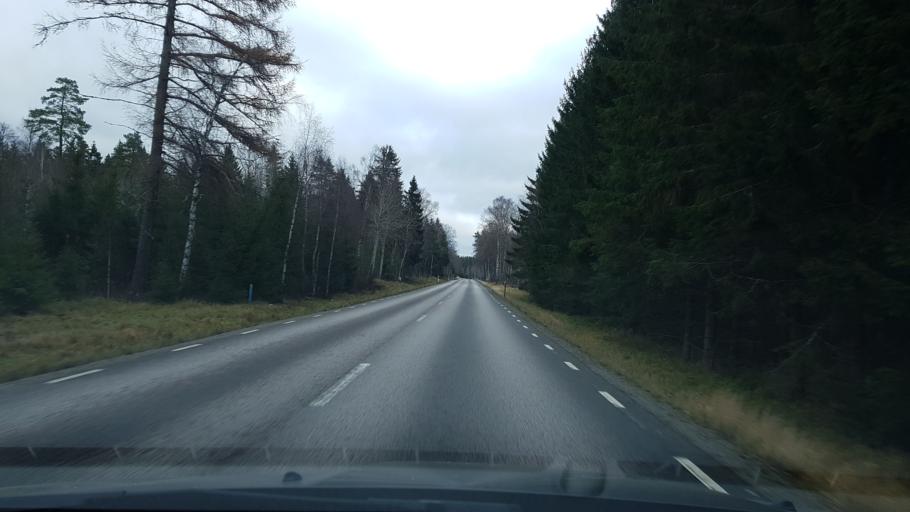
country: SE
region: Stockholm
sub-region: Norrtalje Kommun
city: Hallstavik
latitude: 60.0400
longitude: 18.5318
